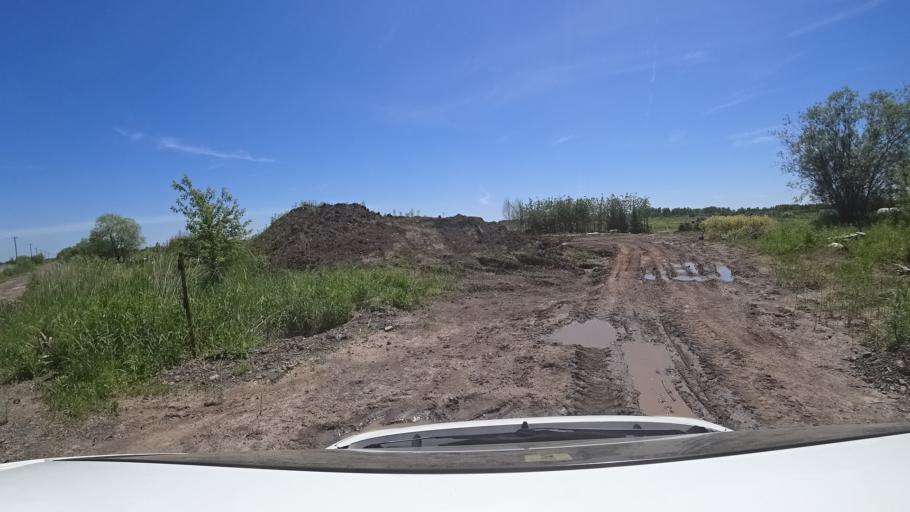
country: RU
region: Khabarovsk Krai
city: Topolevo
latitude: 48.4992
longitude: 135.2043
